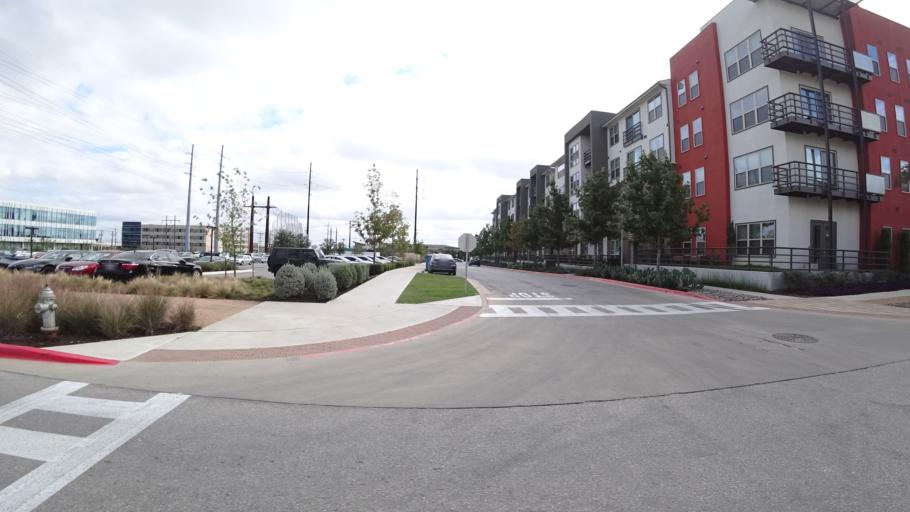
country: US
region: Texas
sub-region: Travis County
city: Wells Branch
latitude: 30.3972
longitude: -97.7213
